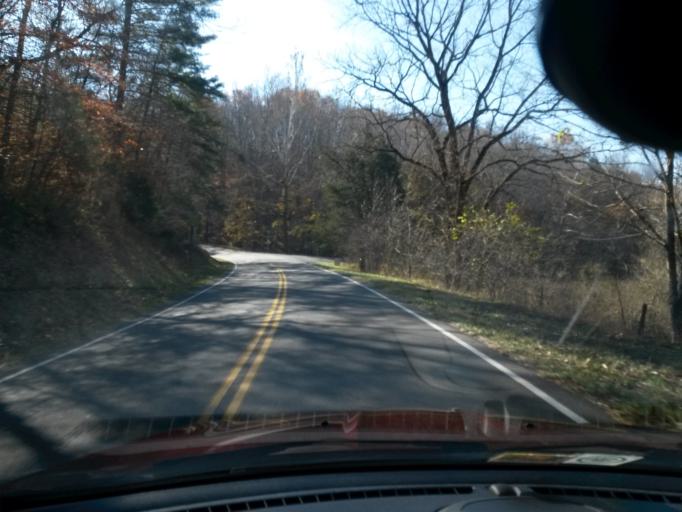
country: US
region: Virginia
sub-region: Botetourt County
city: Buchanan
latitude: 37.6150
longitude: -79.7384
